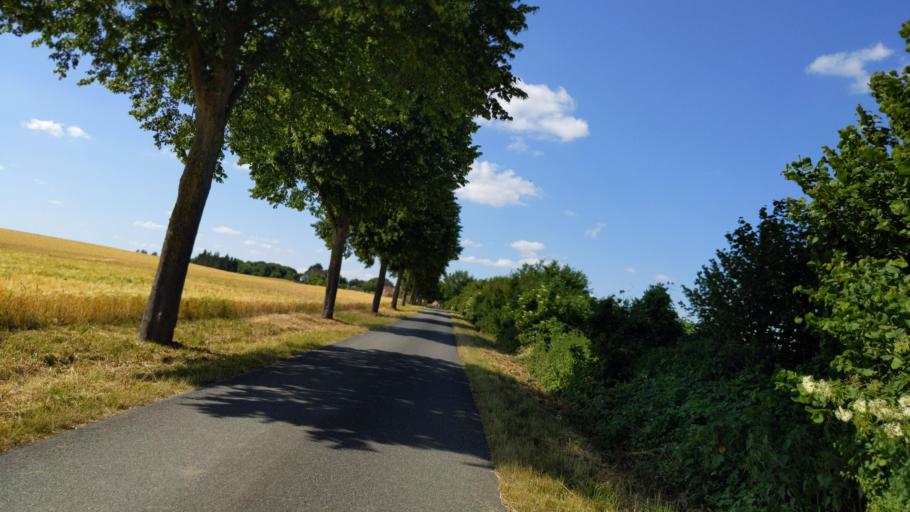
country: DE
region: Schleswig-Holstein
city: Kulpin
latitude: 53.7042
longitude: 10.7040
